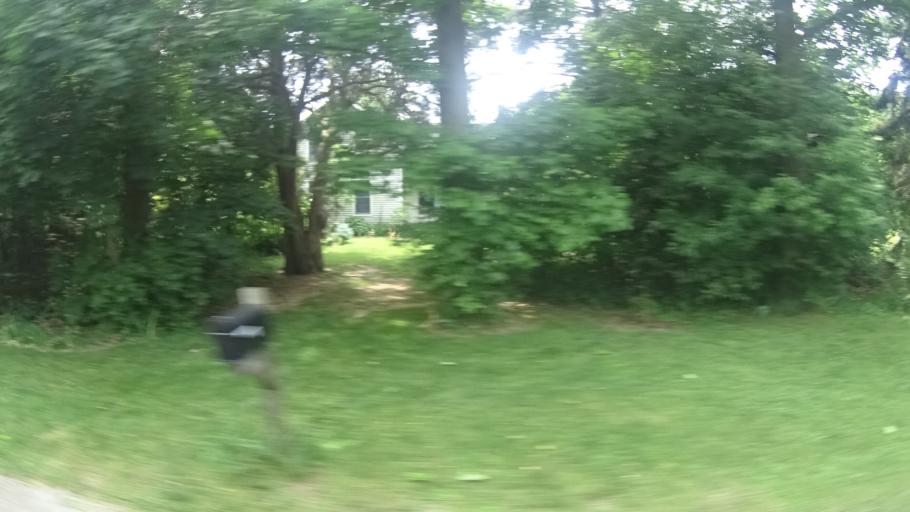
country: US
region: Ohio
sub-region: Erie County
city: Milan
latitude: 41.3116
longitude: -82.6655
